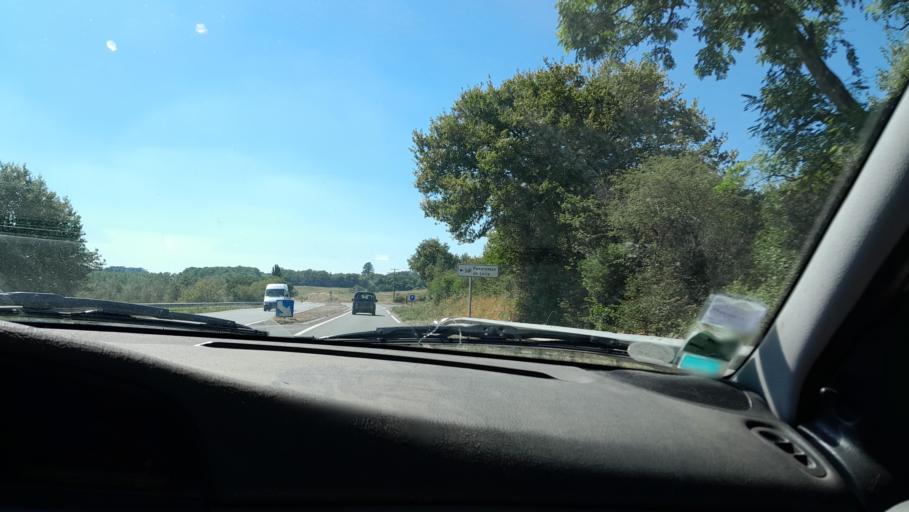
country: FR
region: Pays de la Loire
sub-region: Departement de la Loire-Atlantique
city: Oudon
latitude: 47.3529
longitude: -1.2672
